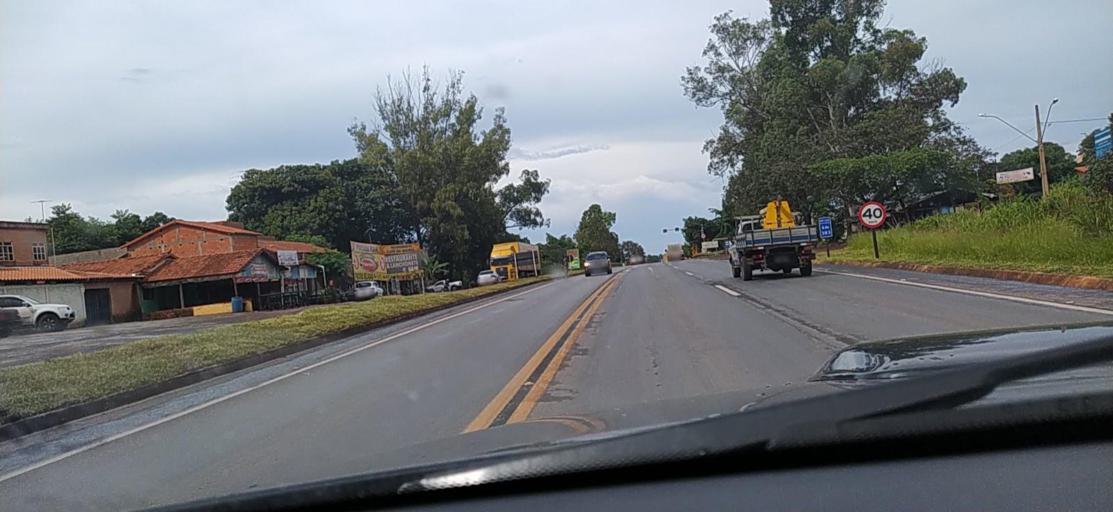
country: BR
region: Minas Gerais
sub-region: Montes Claros
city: Montes Claros
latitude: -16.8801
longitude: -43.8637
